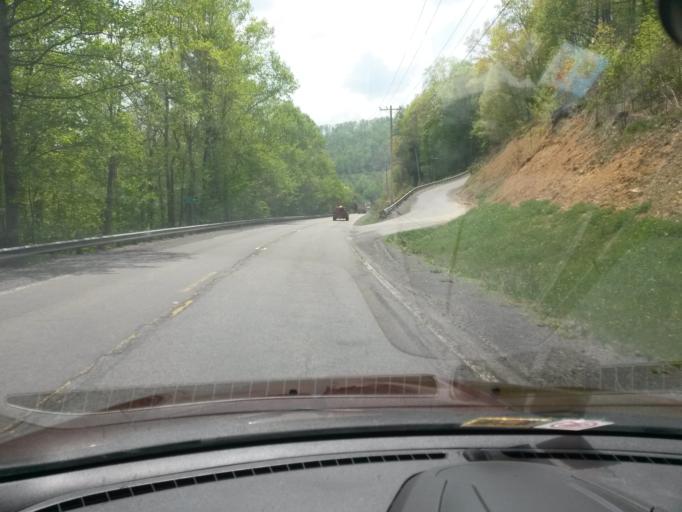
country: US
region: West Virginia
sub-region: Greenbrier County
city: Rainelle
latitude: 38.0062
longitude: -80.7323
